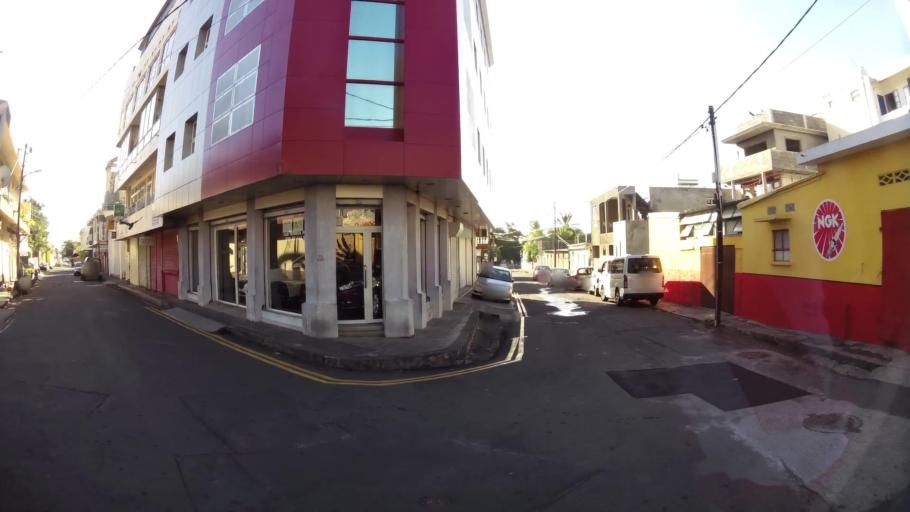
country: MU
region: Port Louis
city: Port Louis
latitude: -20.1672
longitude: 57.4872
